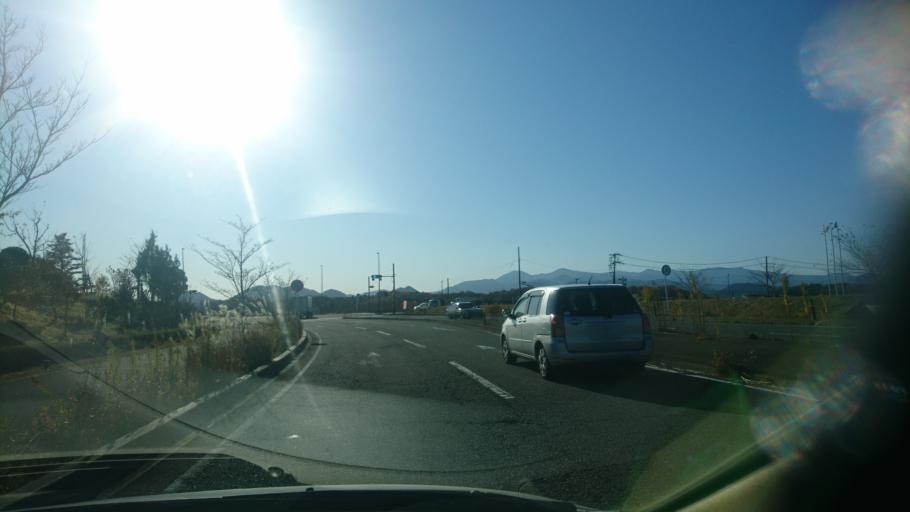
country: JP
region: Miyagi
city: Tomiya
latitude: 38.4739
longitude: 140.8935
